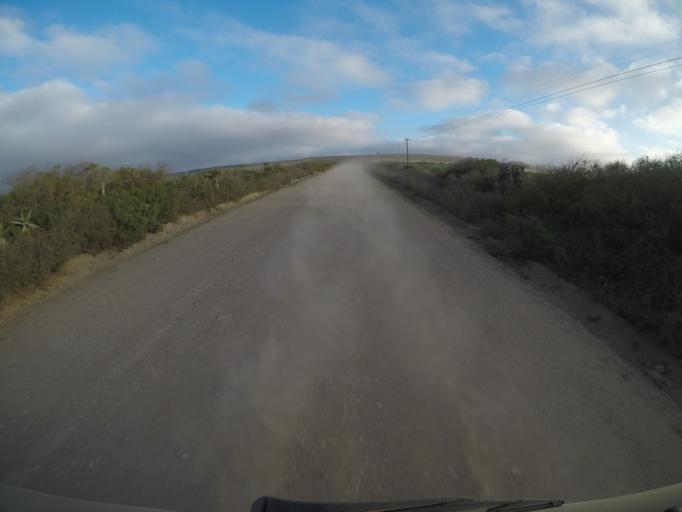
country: ZA
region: Western Cape
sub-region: Eden District Municipality
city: Mossel Bay
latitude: -34.1198
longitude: 22.0534
